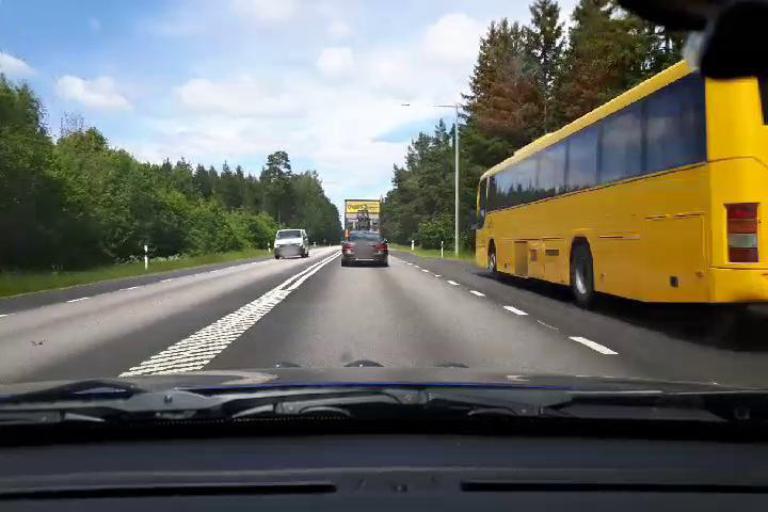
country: SE
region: Uppsala
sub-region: Osthammars Kommun
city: Bjorklinge
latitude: 60.0432
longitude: 17.5507
